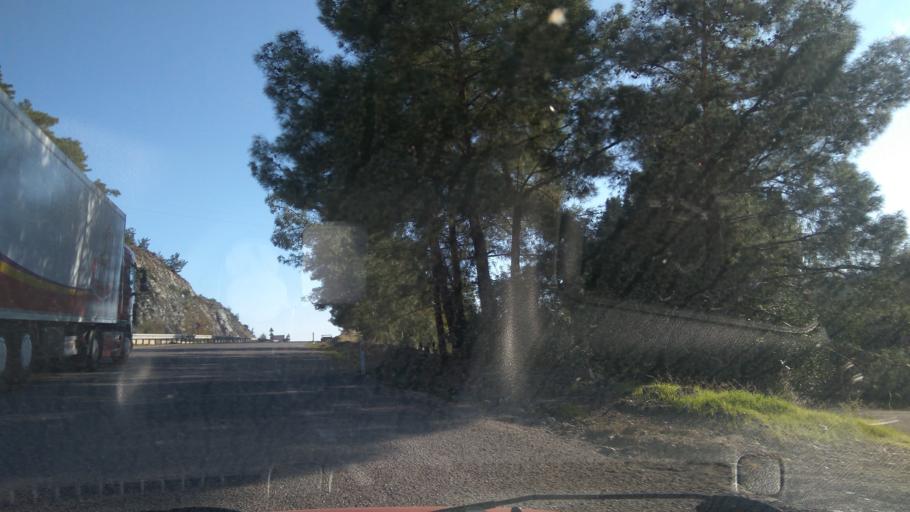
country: TR
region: Antalya
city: Kemer
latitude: 36.5808
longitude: 30.5549
